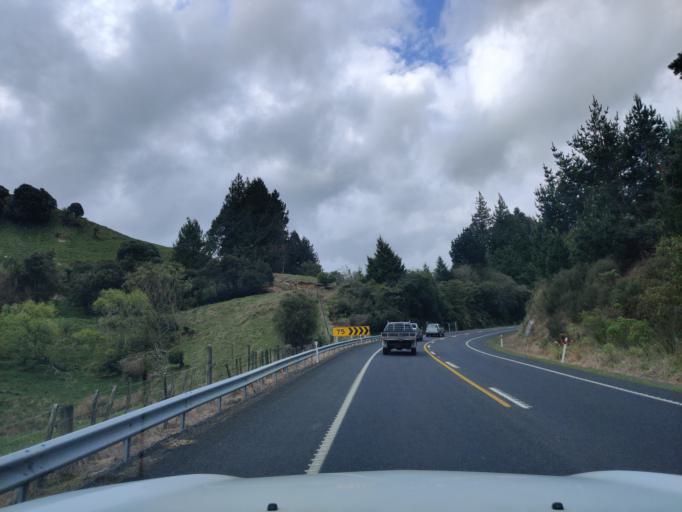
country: NZ
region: Manawatu-Wanganui
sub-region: Ruapehu District
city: Waiouru
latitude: -39.4917
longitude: 175.2936
